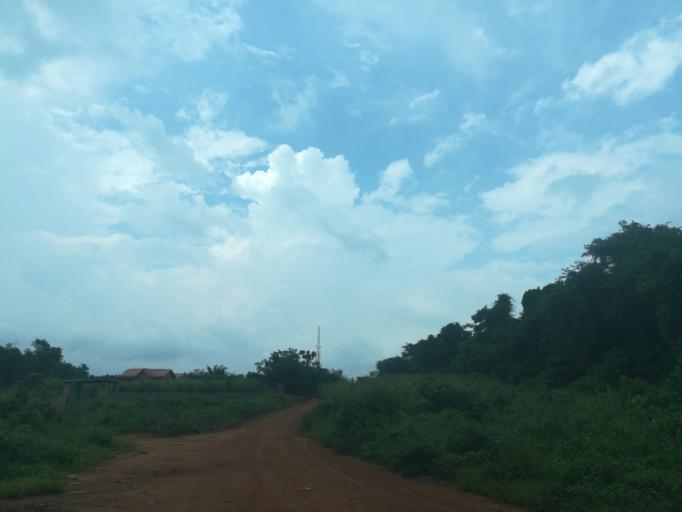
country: NG
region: Lagos
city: Ikorodu
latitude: 6.6632
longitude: 3.6325
